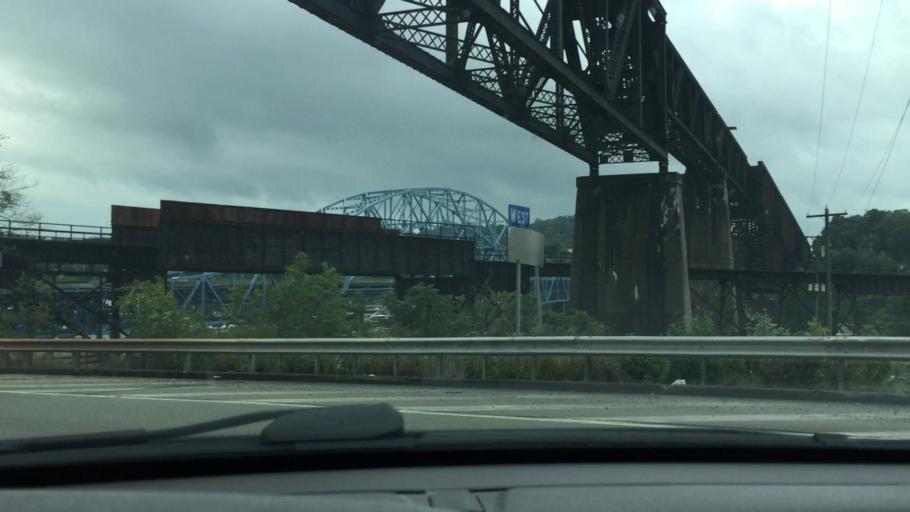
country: US
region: Pennsylvania
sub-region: Washington County
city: Speers
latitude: 40.1299
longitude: -79.8774
